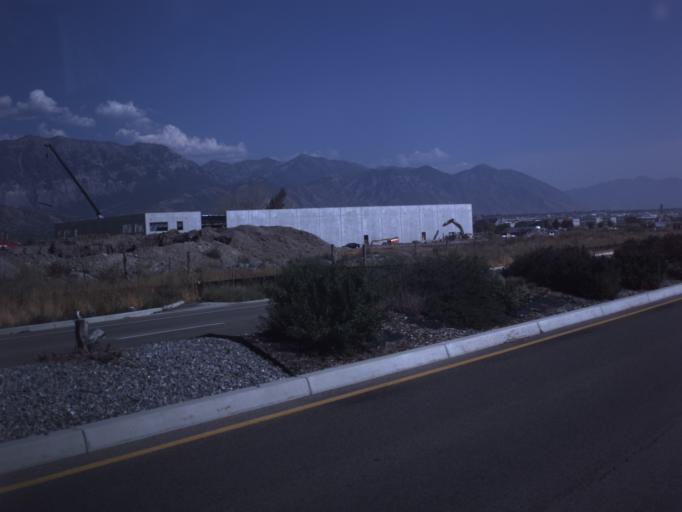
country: US
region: Utah
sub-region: Utah County
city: Pleasant Grove
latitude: 40.3575
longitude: -111.7680
